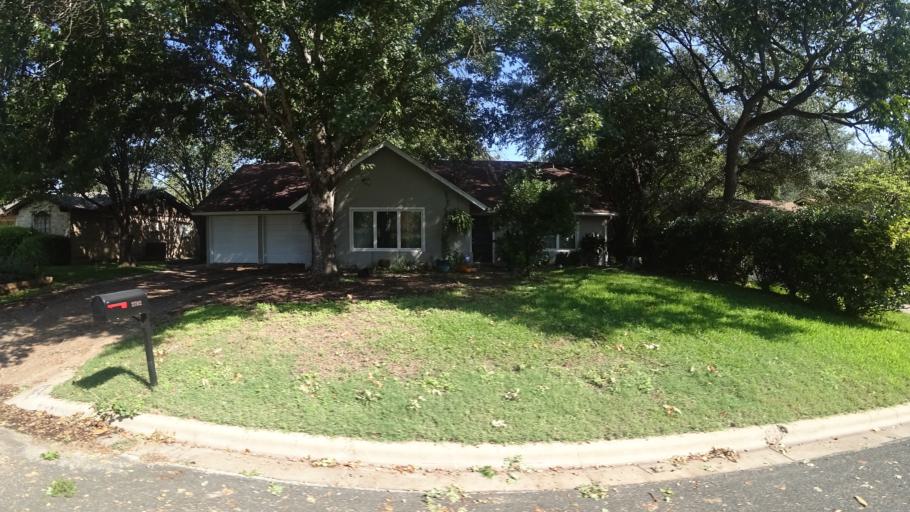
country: US
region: Texas
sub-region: Travis County
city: Austin
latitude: 30.3175
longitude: -97.6734
